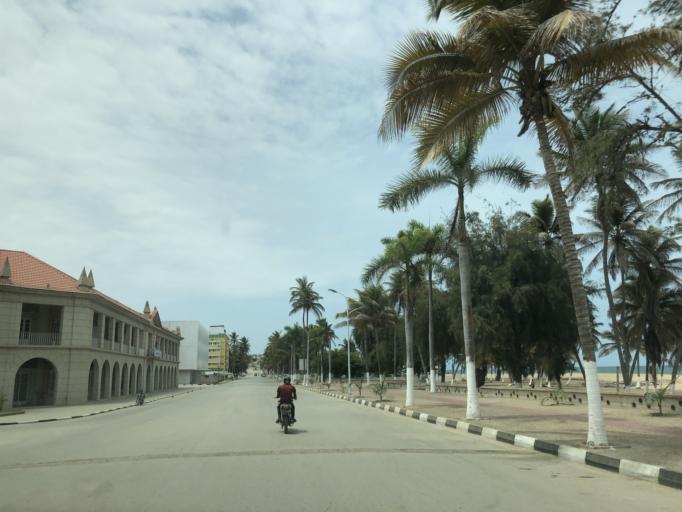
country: AO
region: Cuanza Sul
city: Sumbe
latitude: -11.1955
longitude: 13.8355
